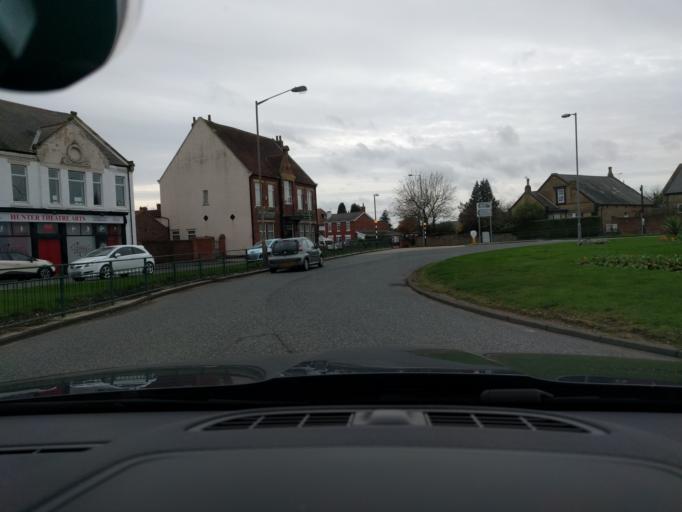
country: GB
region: England
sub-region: Northumberland
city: Choppington
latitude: 55.1586
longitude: -1.6029
